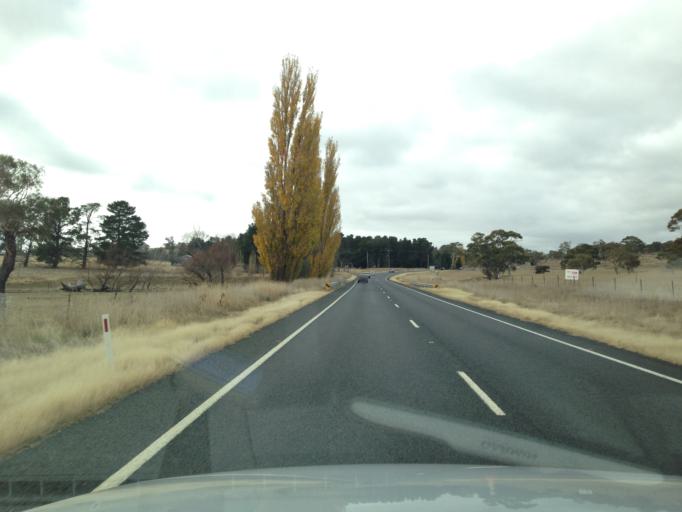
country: AU
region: New South Wales
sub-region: Cooma-Monaro
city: Cooma
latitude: -36.2423
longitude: 149.0637
